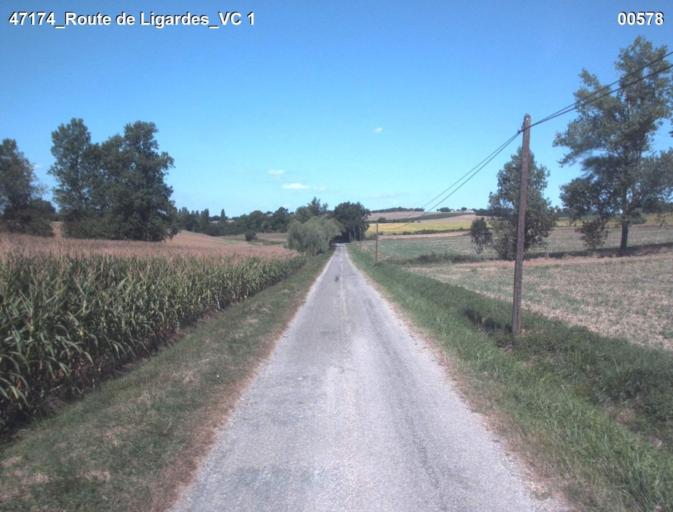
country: FR
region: Midi-Pyrenees
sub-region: Departement du Gers
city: Condom
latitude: 44.0299
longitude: 0.4118
